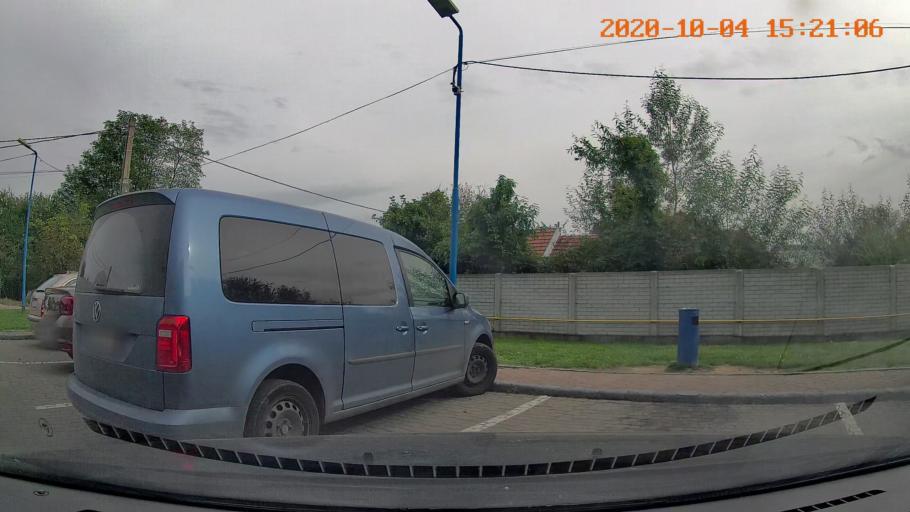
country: RO
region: Caras-Severin
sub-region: Comuna Glimboca
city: Glimboca
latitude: 45.5079
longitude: 22.3419
